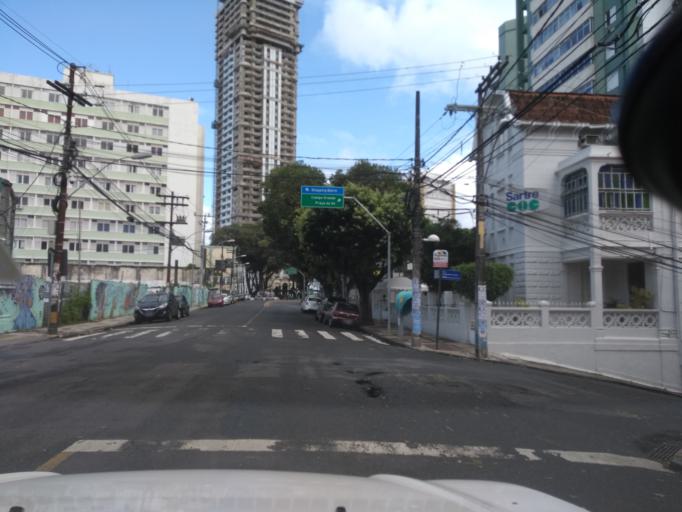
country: BR
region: Bahia
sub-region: Salvador
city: Salvador
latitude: -12.9970
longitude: -38.5264
